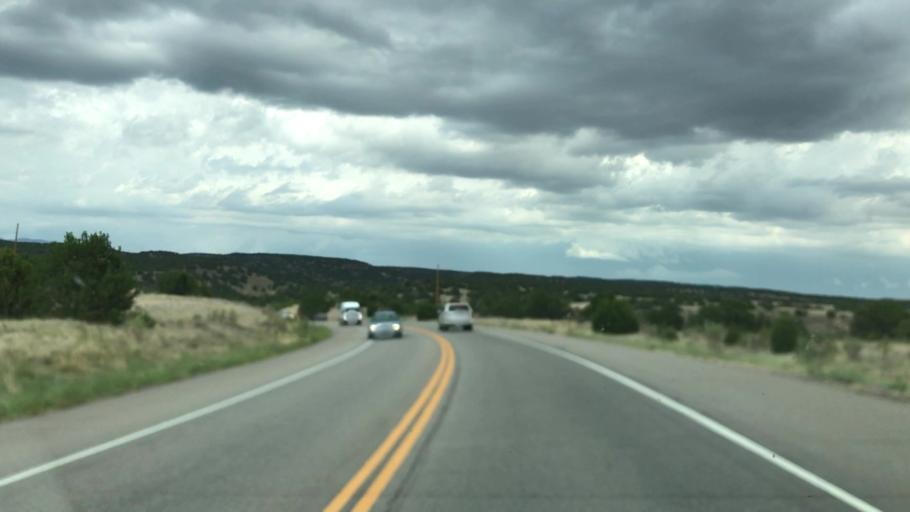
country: US
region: Colorado
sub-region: Fremont County
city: Penrose
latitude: 38.4837
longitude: -104.9633
